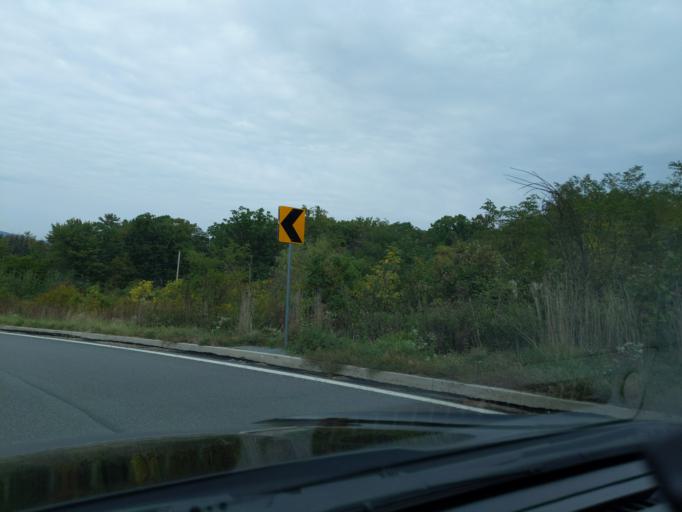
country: US
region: Pennsylvania
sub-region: Blair County
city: Lakemont
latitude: 40.4801
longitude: -78.3893
